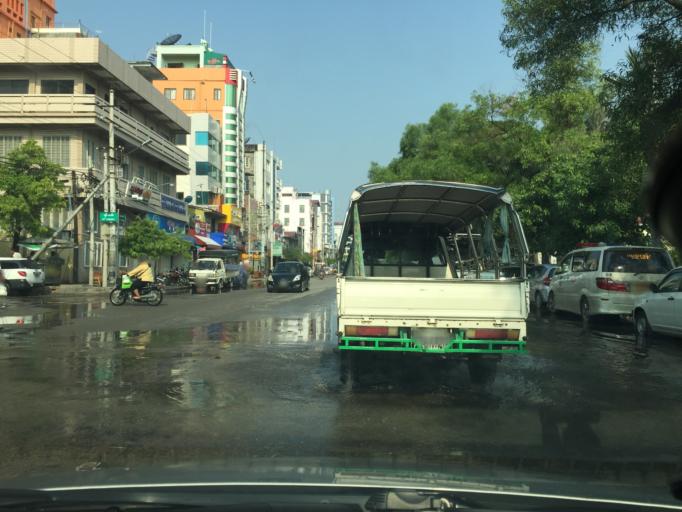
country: MM
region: Mandalay
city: Mandalay
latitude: 21.9767
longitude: 96.0907
